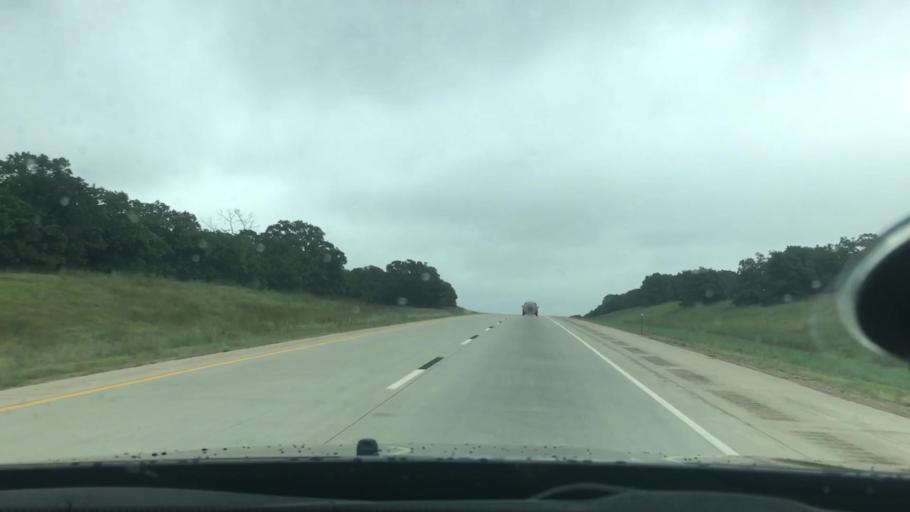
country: US
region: Oklahoma
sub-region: Okfuskee County
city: Boley
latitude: 35.3835
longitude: -96.5111
